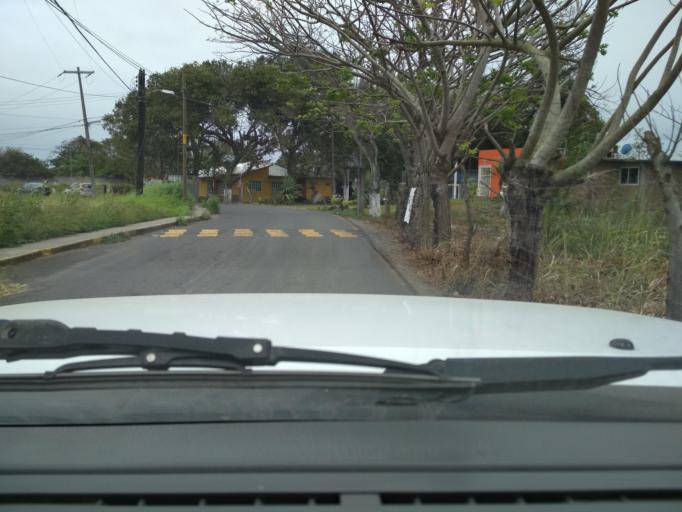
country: MX
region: Veracruz
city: Paso del Toro
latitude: 19.0548
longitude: -96.1336
